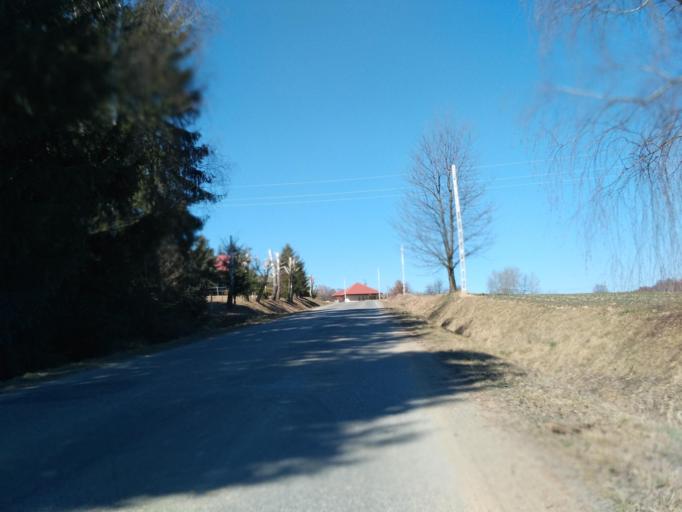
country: PL
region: Subcarpathian Voivodeship
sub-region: Powiat debicki
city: Brzostek
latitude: 49.9395
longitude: 21.4412
